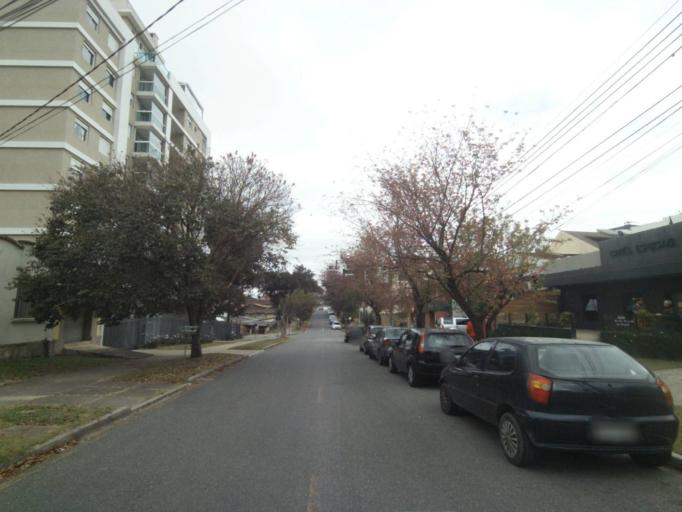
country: BR
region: Parana
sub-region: Curitiba
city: Curitiba
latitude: -25.4549
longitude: -49.2908
